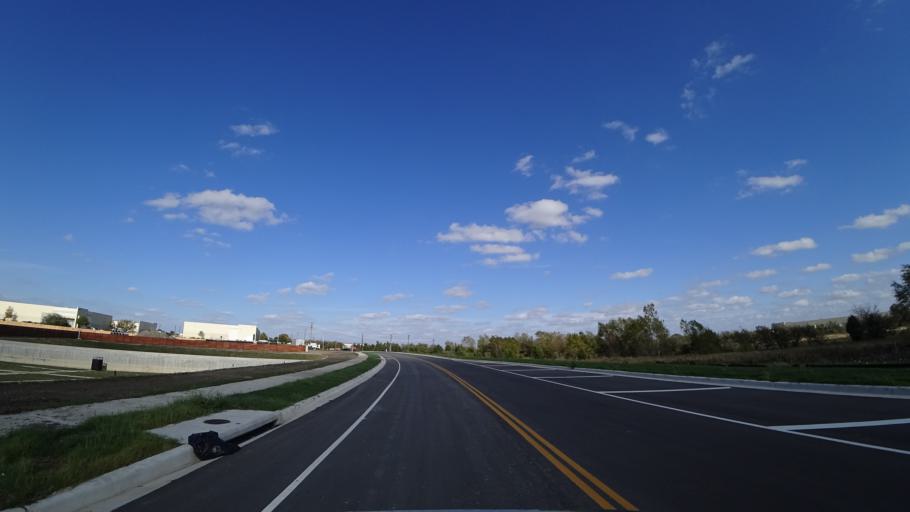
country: US
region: Texas
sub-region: Travis County
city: Wells Branch
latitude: 30.4651
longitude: -97.6783
